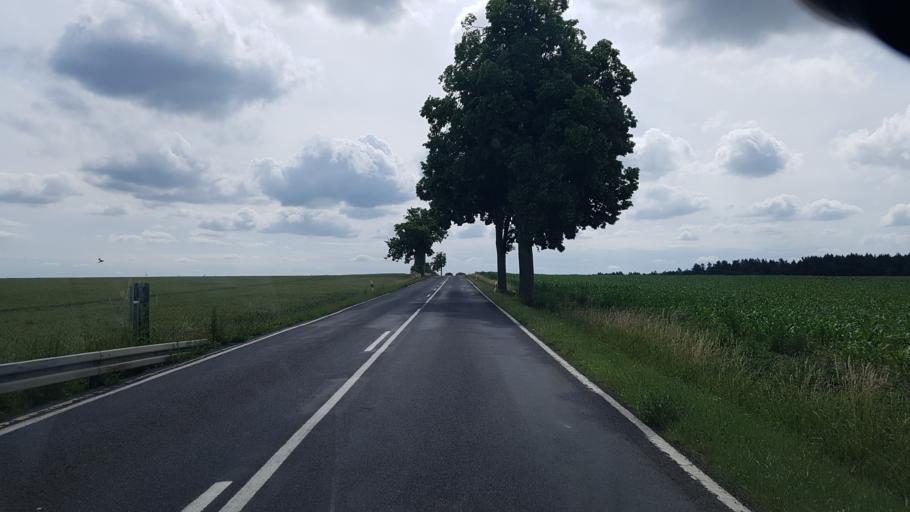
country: DE
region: Mecklenburg-Vorpommern
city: Strasburg
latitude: 53.4143
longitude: 13.7214
